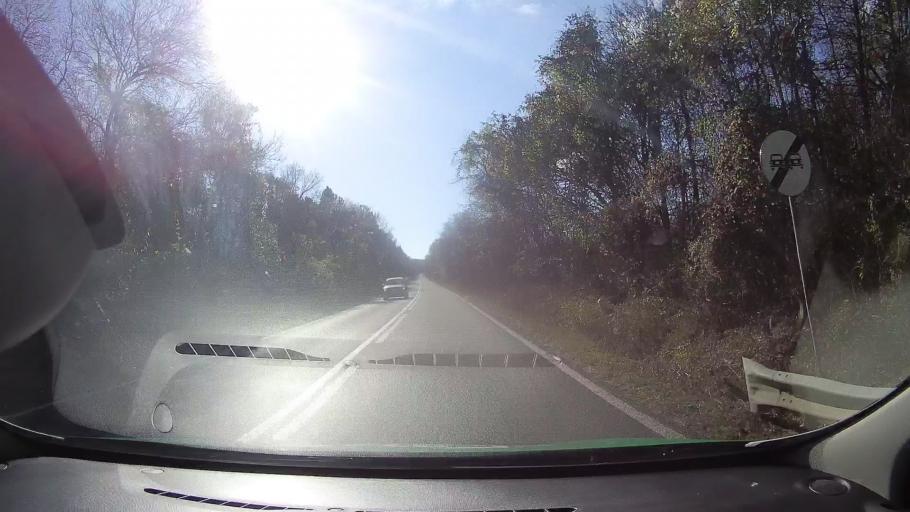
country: RO
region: Tulcea
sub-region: Oras Babadag
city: Babadag
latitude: 44.8384
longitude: 28.6958
